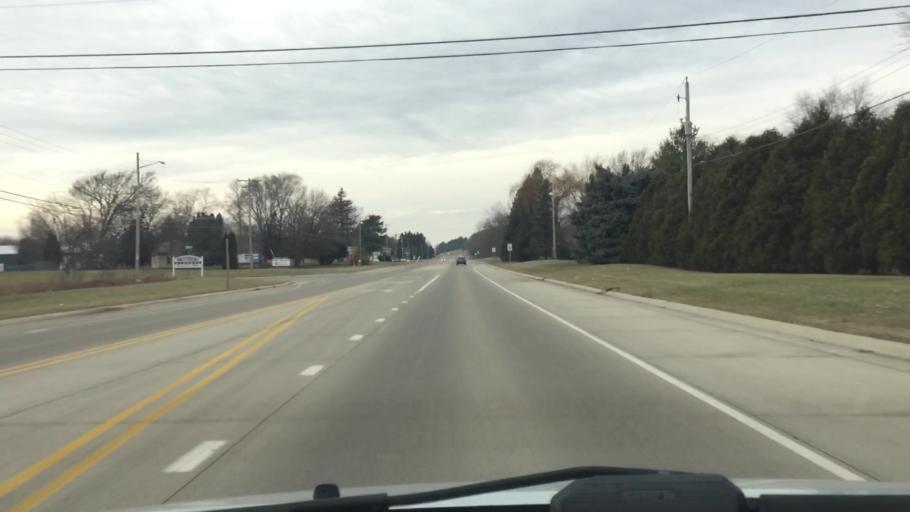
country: US
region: Wisconsin
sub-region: Waukesha County
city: Oconomowoc
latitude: 43.1257
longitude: -88.5322
